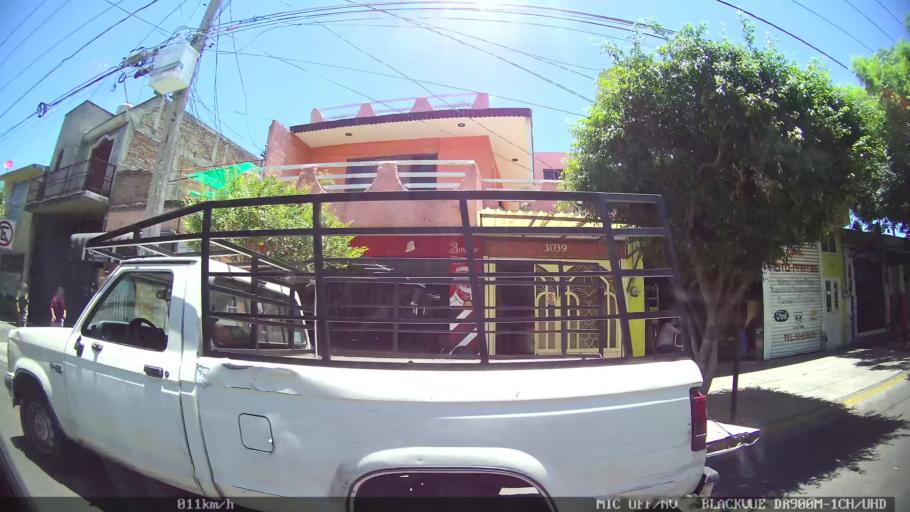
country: MX
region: Jalisco
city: Tlaquepaque
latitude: 20.6725
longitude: -103.2929
